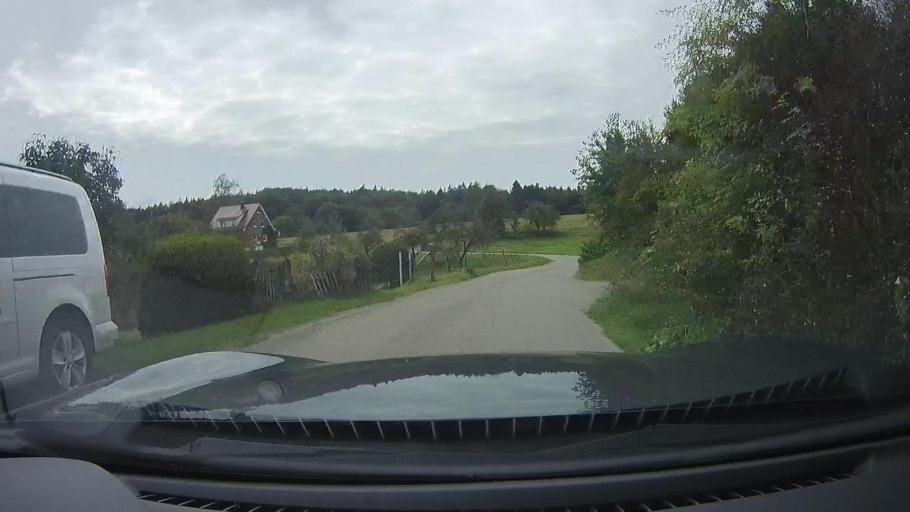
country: DE
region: Baden-Wuerttemberg
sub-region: Regierungsbezirk Stuttgart
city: Sulzbach an der Murr
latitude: 48.9853
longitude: 9.5057
